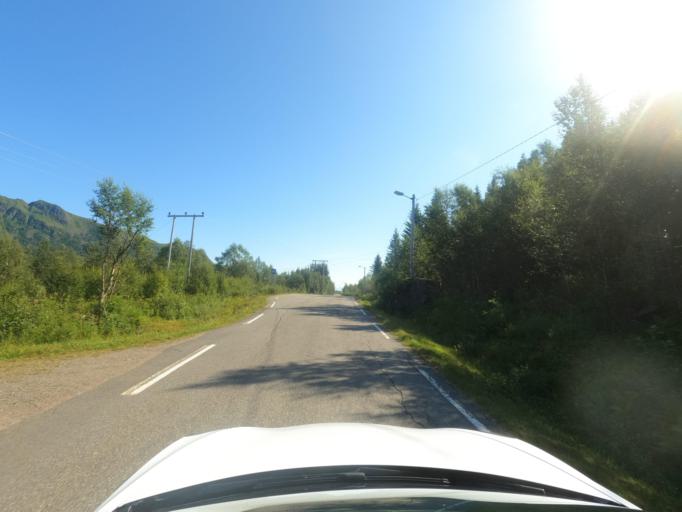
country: NO
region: Nordland
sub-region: Hadsel
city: Stokmarknes
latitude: 68.2990
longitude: 15.0468
